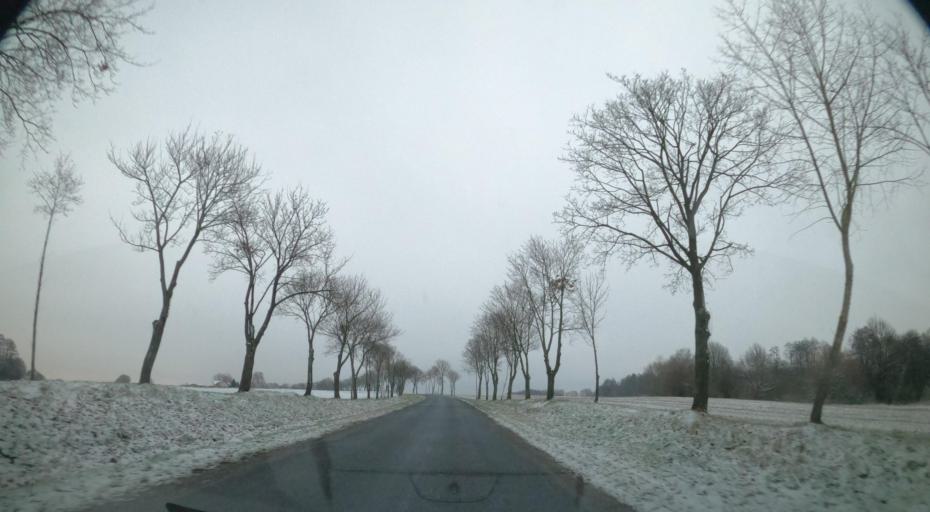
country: PL
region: Kujawsko-Pomorskie
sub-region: Powiat lipnowski
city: Wielgie
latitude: 52.7027
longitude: 19.2877
